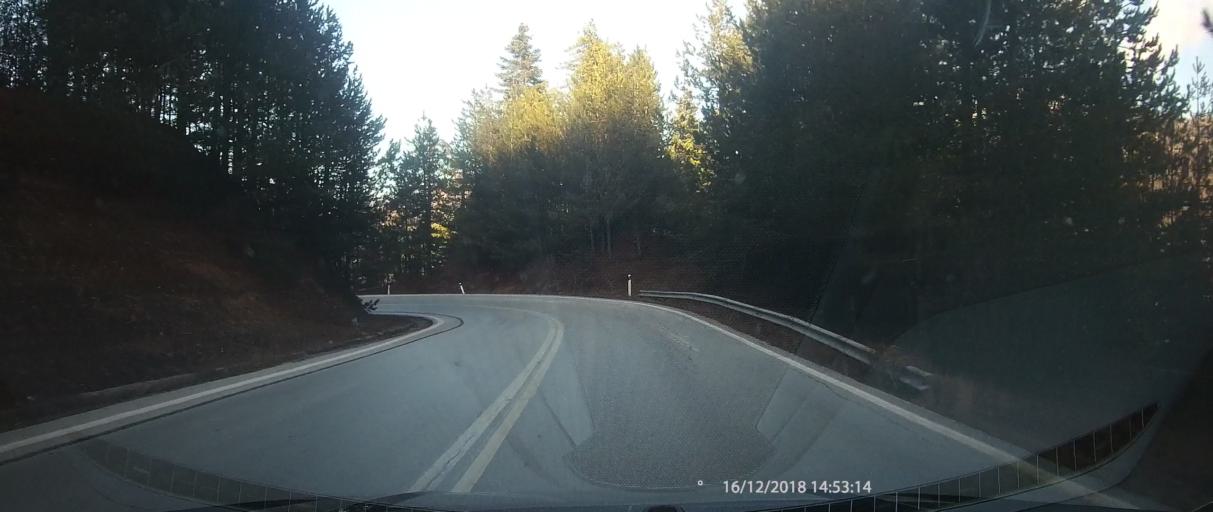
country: GR
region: West Macedonia
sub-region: Nomos Kastorias
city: Nestorio
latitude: 40.2087
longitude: 21.0584
